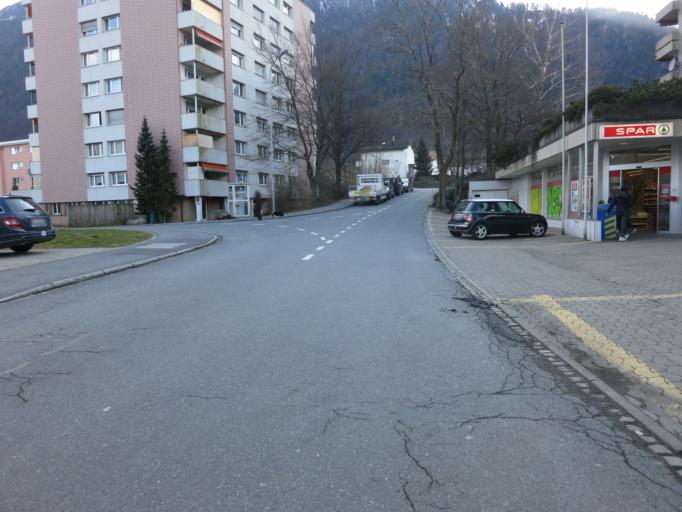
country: CH
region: Glarus
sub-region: Glarus
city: Bilten
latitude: 47.1520
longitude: 9.0257
